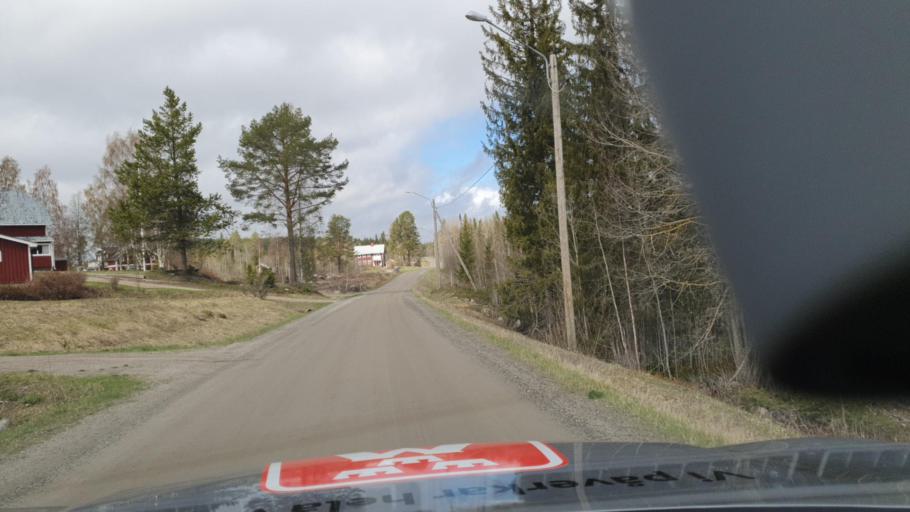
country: SE
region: Vaesterbotten
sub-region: Bjurholms Kommun
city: Bjurholm
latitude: 63.6703
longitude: 19.0010
